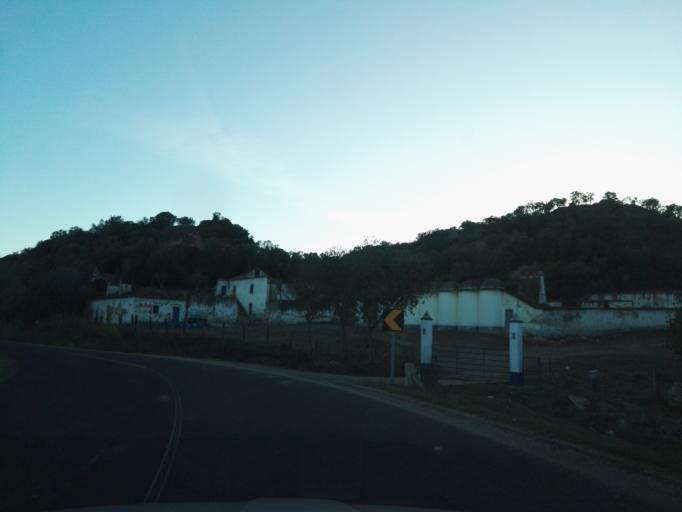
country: PT
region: Santarem
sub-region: Alpiarca
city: Alpiarca
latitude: 39.3329
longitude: -8.5916
